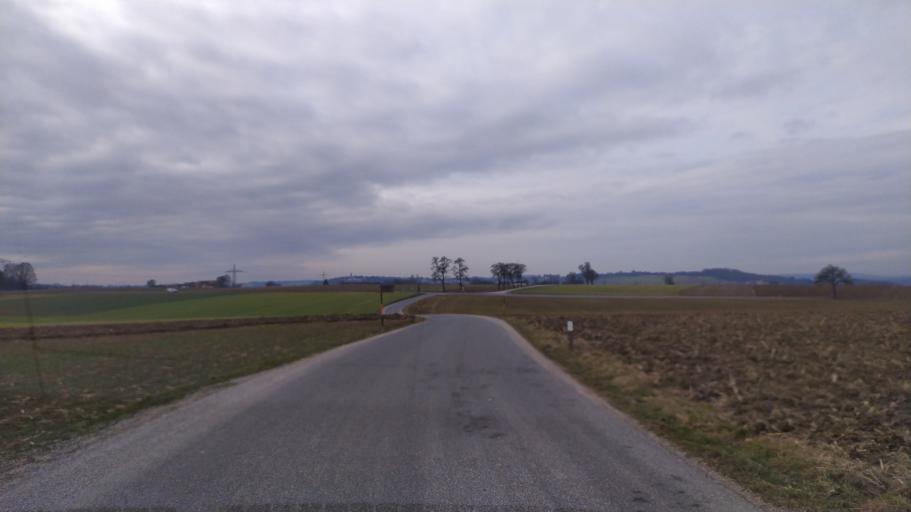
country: AT
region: Lower Austria
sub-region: Politischer Bezirk Amstetten
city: Strengberg
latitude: 48.1476
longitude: 14.7017
